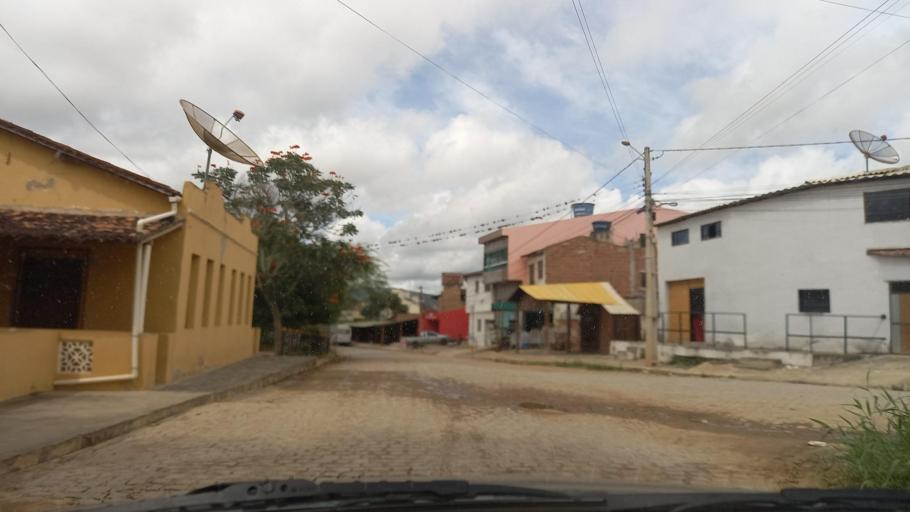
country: BR
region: Pernambuco
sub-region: Gravata
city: Gravata
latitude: -8.1879
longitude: -35.5790
